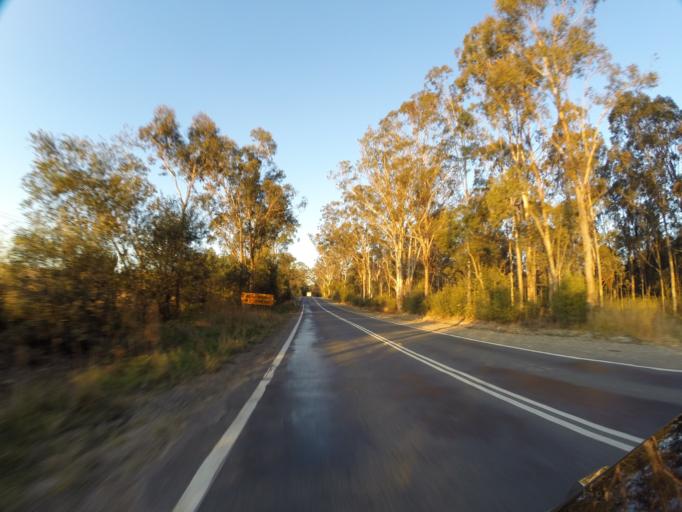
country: AU
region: New South Wales
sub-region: Camden
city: Narellan
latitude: -34.0145
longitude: 150.7118
